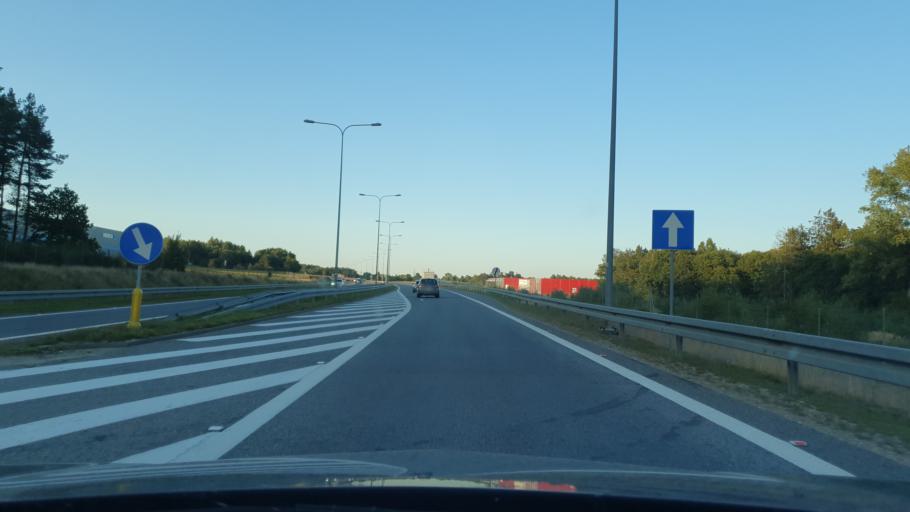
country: PL
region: Pomeranian Voivodeship
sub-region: Slupsk
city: Slupsk
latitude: 54.4440
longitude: 17.0782
